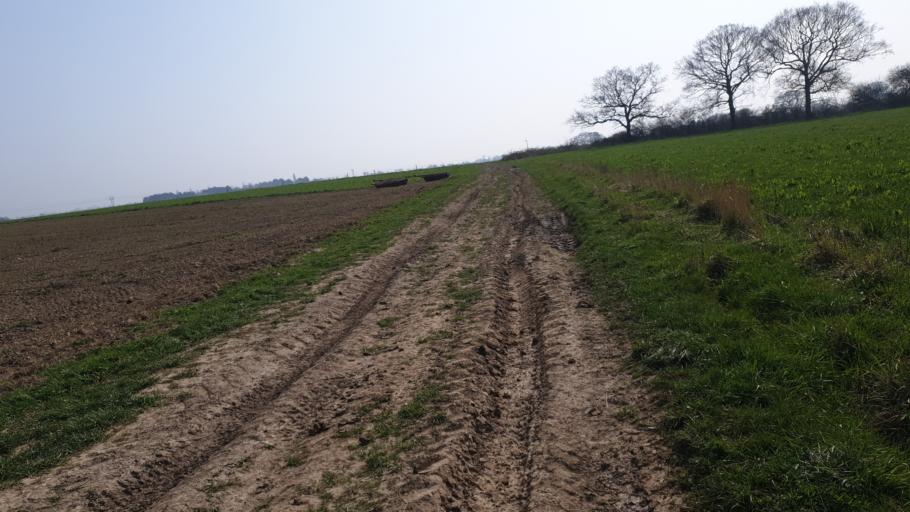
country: GB
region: England
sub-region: Essex
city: Mistley
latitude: 51.9264
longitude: 1.1595
